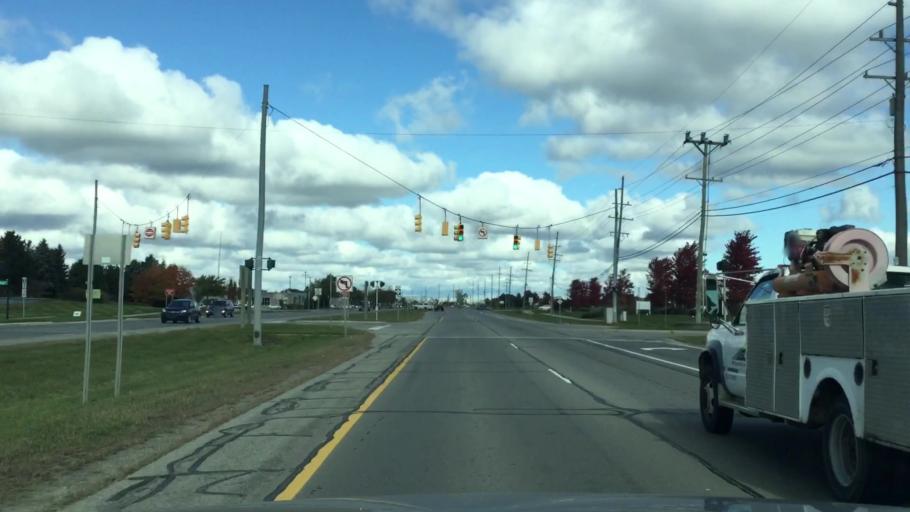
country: US
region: Michigan
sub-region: Oakland County
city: Oxford
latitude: 42.8355
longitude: -83.2716
